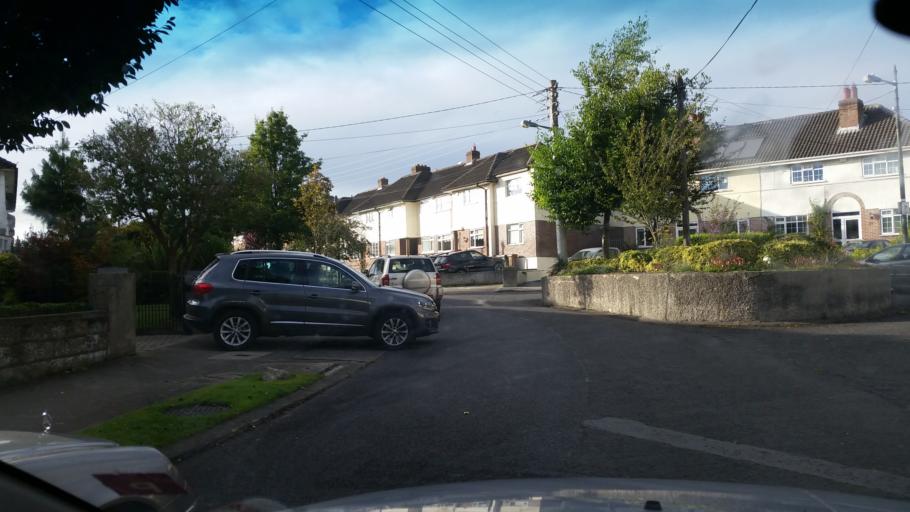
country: IE
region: Leinster
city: Glasnevin
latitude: 53.3800
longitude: -6.2628
